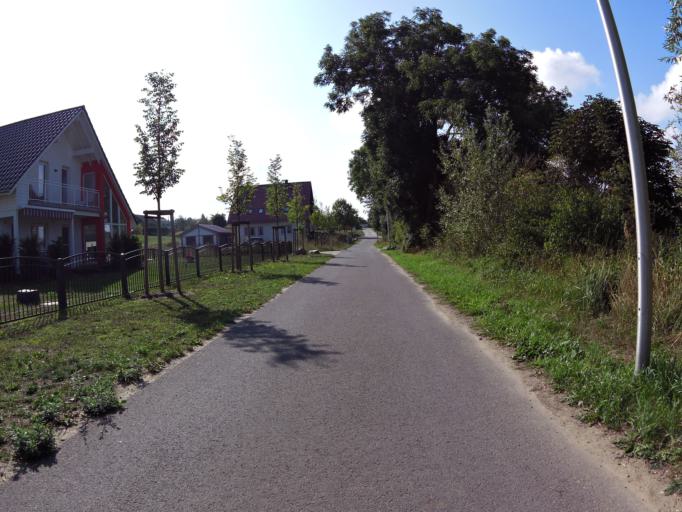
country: DE
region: Mecklenburg-Vorpommern
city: Loddin
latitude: 53.9712
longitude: 14.0642
